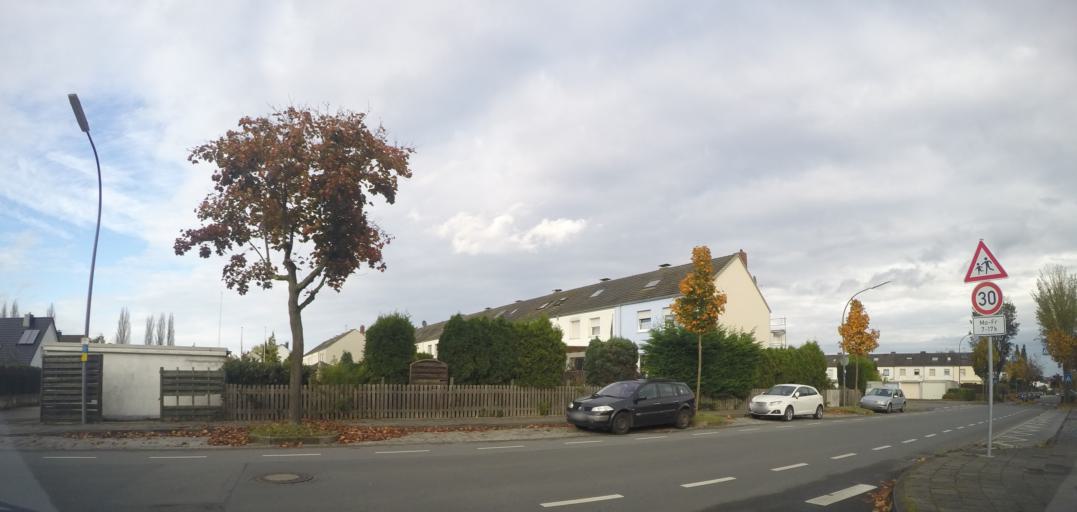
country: DE
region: North Rhine-Westphalia
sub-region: Regierungsbezirk Arnsberg
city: Lippstadt
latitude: 51.6655
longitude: 8.3298
